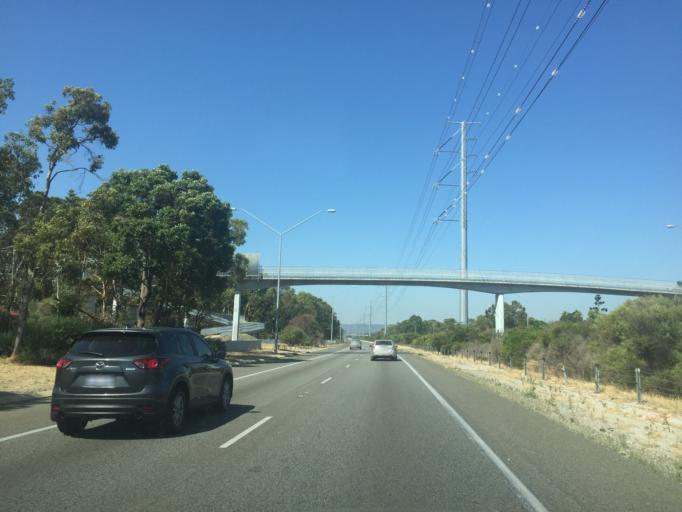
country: AU
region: Western Australia
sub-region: Gosnells
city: Langford
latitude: -32.0508
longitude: 115.9382
